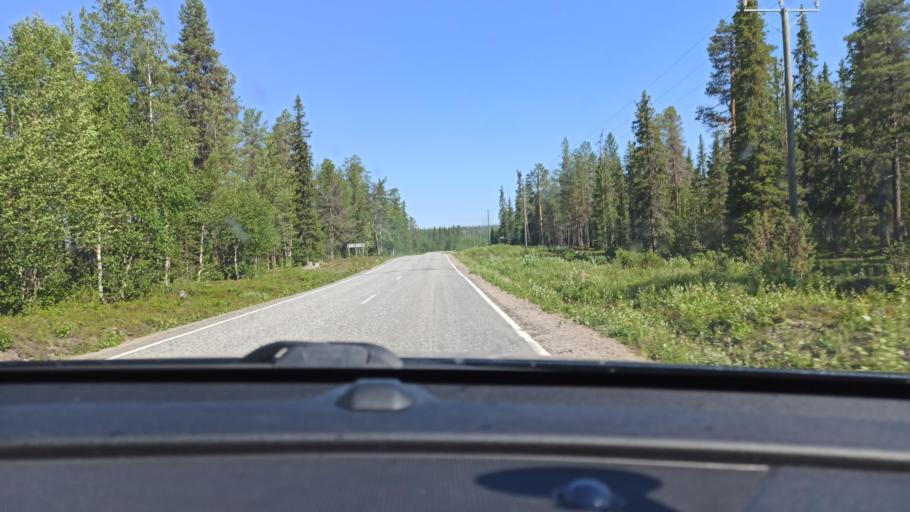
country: FI
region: Lapland
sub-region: Tunturi-Lappi
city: Kolari
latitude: 67.6272
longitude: 24.1557
